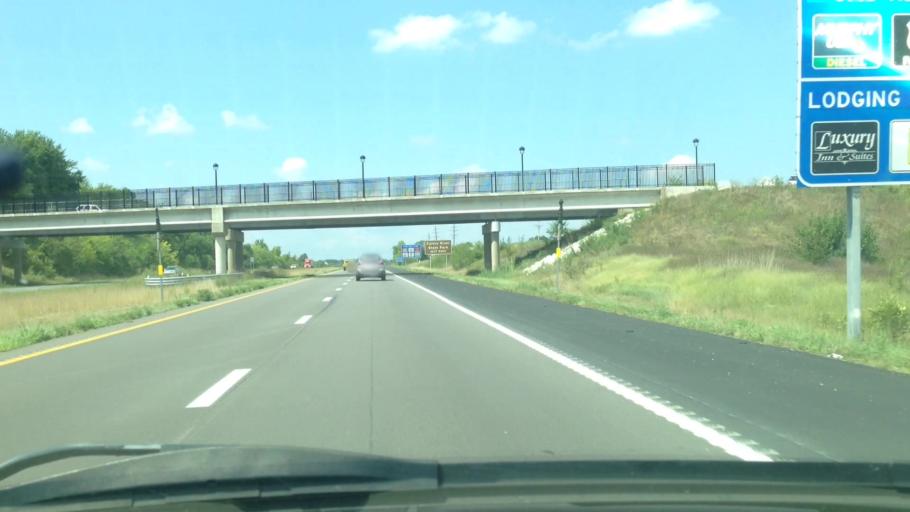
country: US
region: Missouri
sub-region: Lincoln County
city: Troy
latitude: 38.9763
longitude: -90.9625
